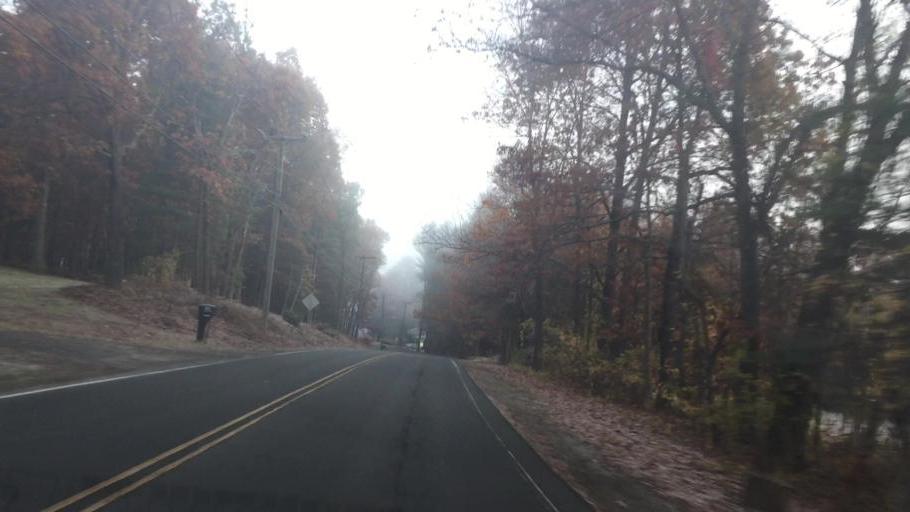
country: US
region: Massachusetts
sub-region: Hampshire County
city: Southampton
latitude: 42.2213
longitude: -72.6886
